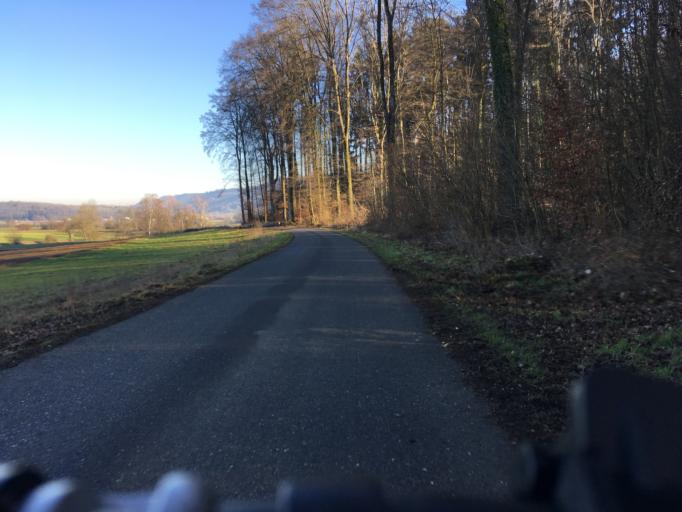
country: CH
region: Schaffhausen
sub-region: Bezirk Stein
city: Ramsen
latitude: 47.7219
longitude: 8.8045
